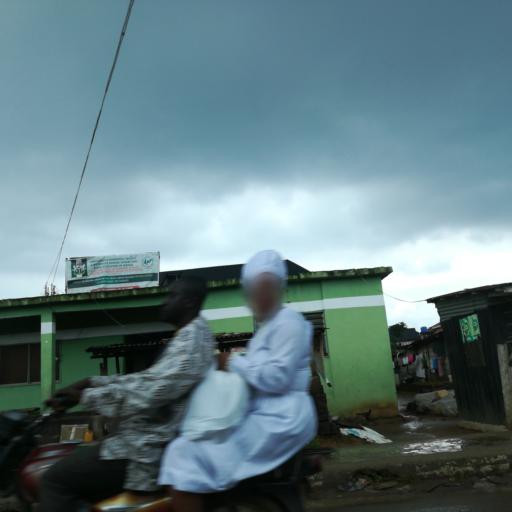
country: NG
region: Lagos
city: Agege
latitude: 6.5886
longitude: 3.2950
